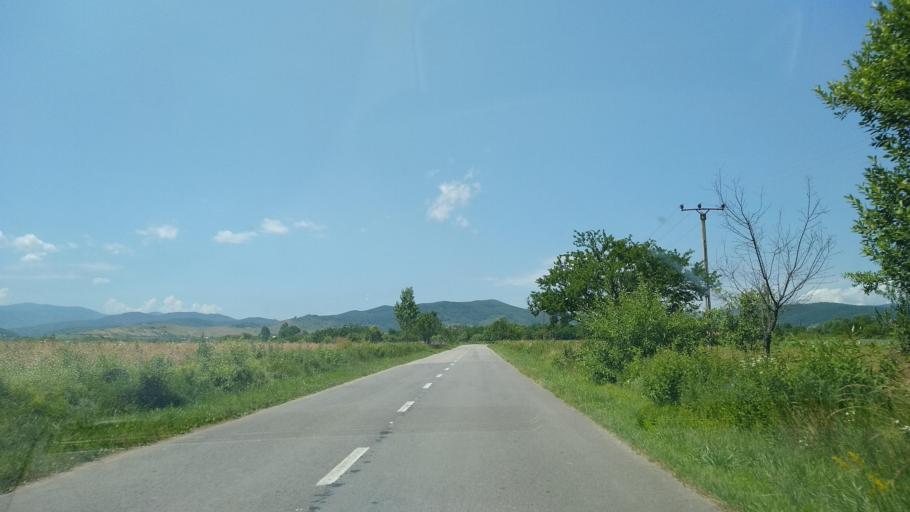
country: RO
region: Hunedoara
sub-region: Comuna Totesti
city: Totesti
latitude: 45.5770
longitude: 22.8453
